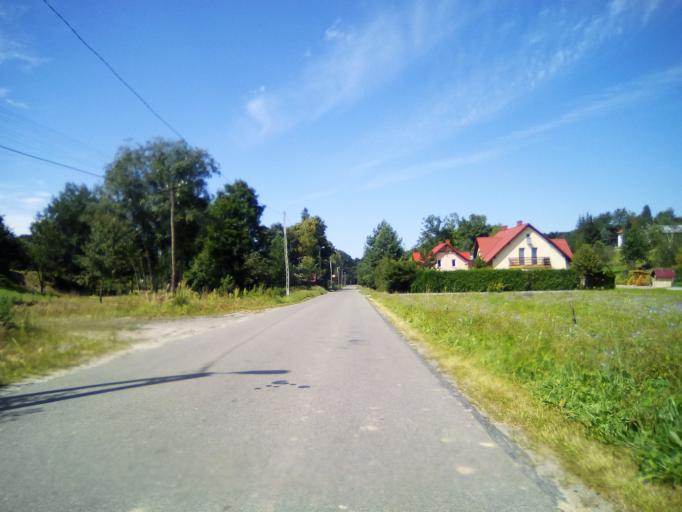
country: PL
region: Subcarpathian Voivodeship
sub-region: Powiat strzyzowski
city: Konieczkowa
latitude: 49.8366
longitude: 21.9298
